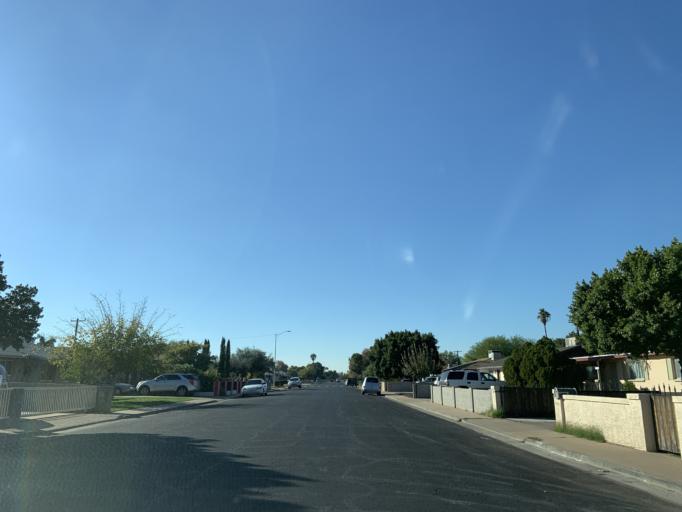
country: US
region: Arizona
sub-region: Maricopa County
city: Mesa
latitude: 33.4029
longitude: -111.8628
